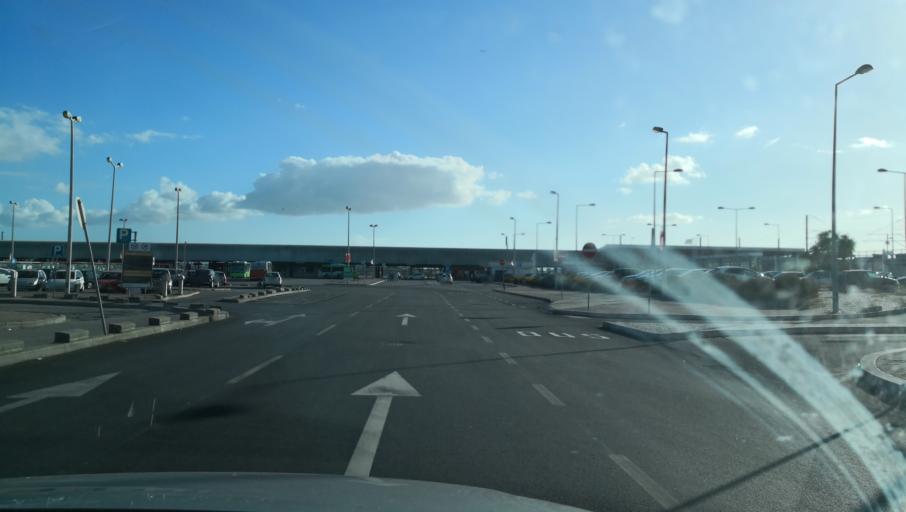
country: PT
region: Setubal
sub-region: Barreiro
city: Barreiro
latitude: 38.6535
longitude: -9.0783
